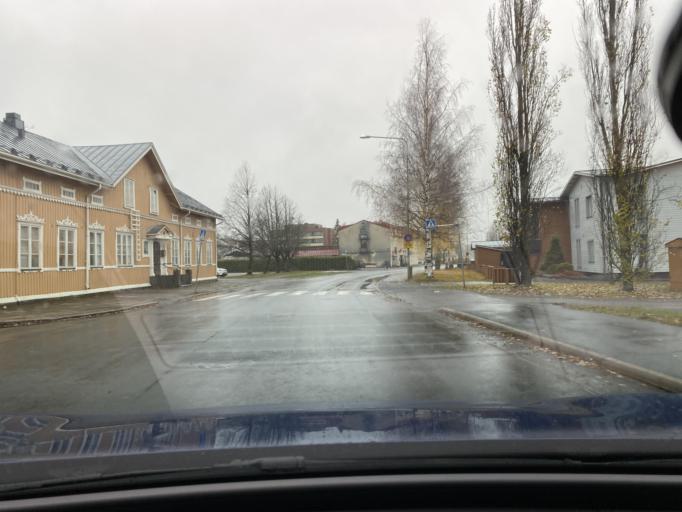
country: FI
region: Varsinais-Suomi
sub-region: Loimaa
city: Loimaa
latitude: 60.8525
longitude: 23.0587
